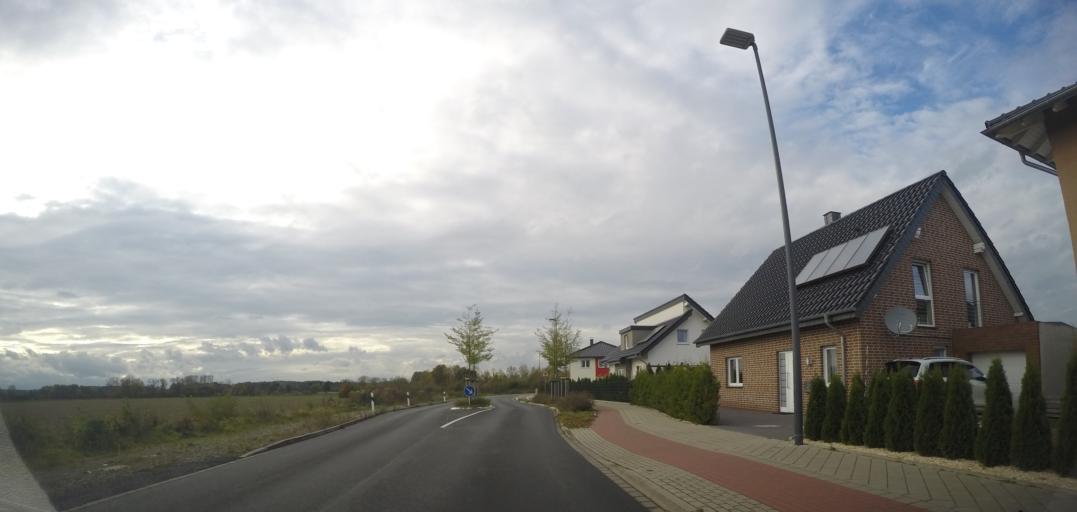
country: DE
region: North Rhine-Westphalia
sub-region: Regierungsbezirk Arnsberg
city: Lippstadt
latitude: 51.6545
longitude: 8.3318
